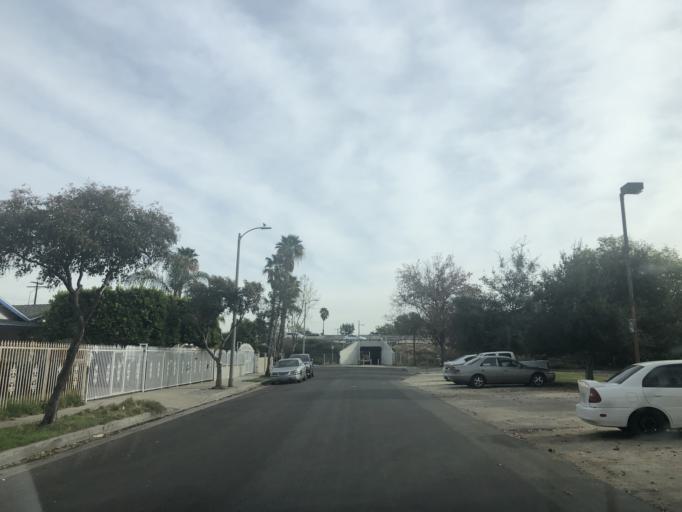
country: US
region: California
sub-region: Los Angeles County
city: San Fernando
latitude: 34.2691
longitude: -118.4372
